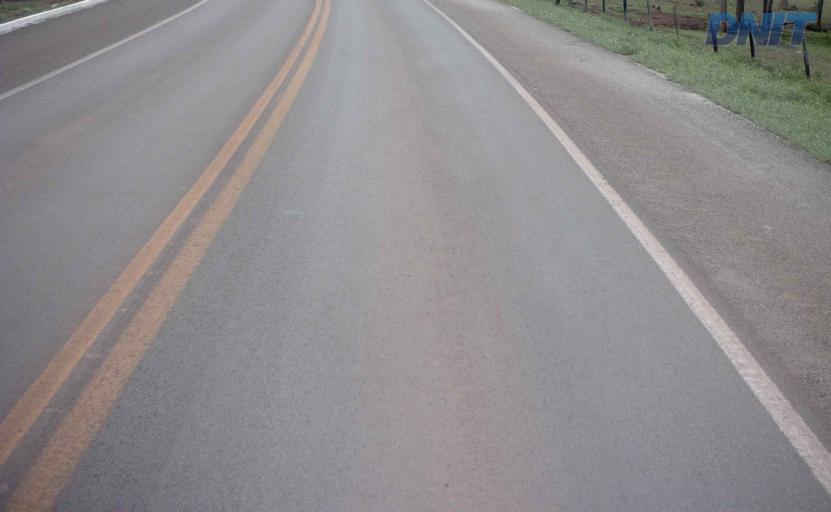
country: BR
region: Goias
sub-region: Padre Bernardo
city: Padre Bernardo
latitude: -15.1633
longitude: -48.3034
